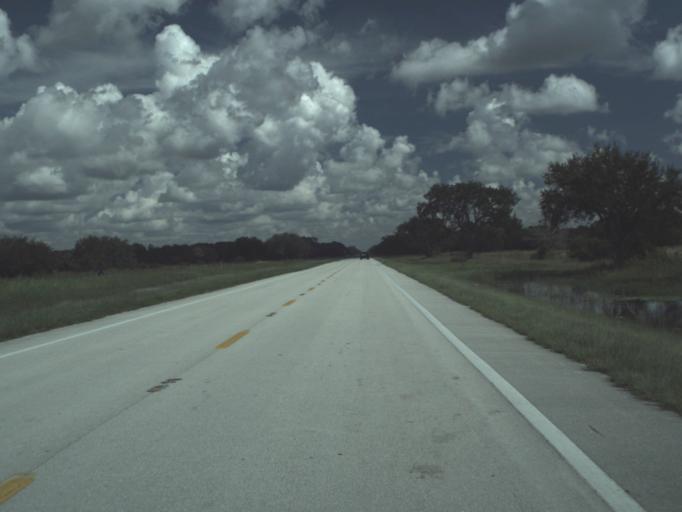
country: US
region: Florida
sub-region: Hendry County
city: Port LaBelle
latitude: 26.8561
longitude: -81.3751
